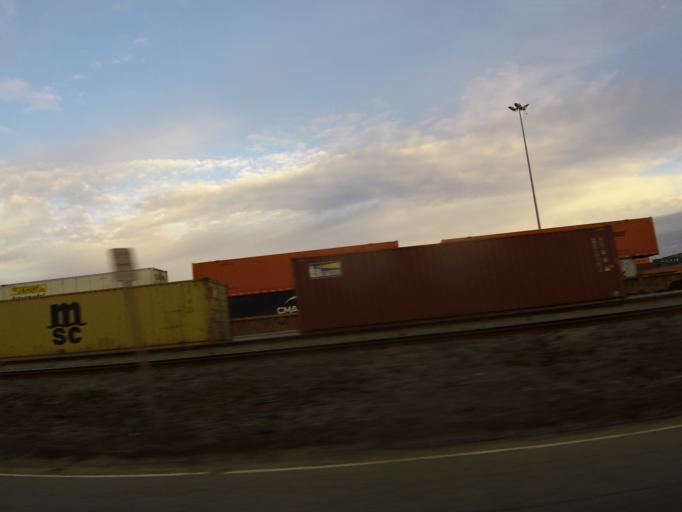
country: US
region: Virginia
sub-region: City of Portsmouth
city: Portsmouth
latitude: 36.8485
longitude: -76.3239
